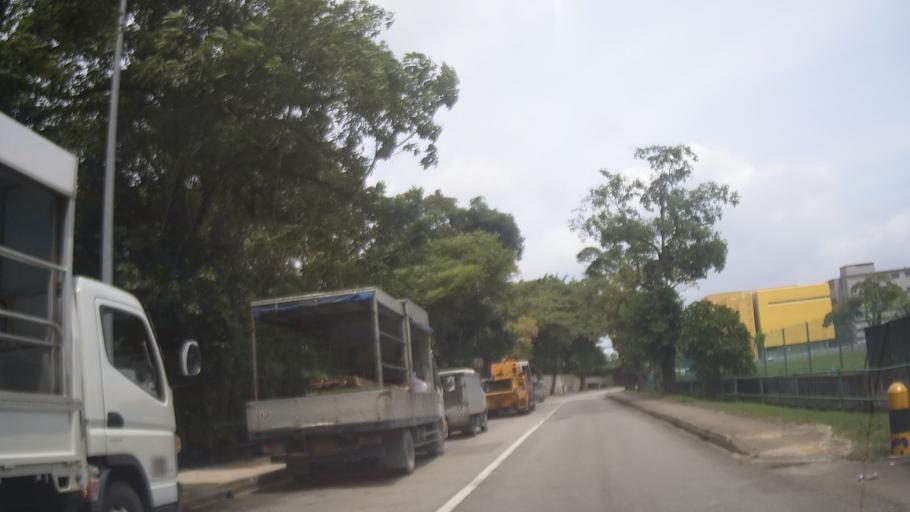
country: MY
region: Johor
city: Johor Bahru
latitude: 1.4129
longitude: 103.7473
